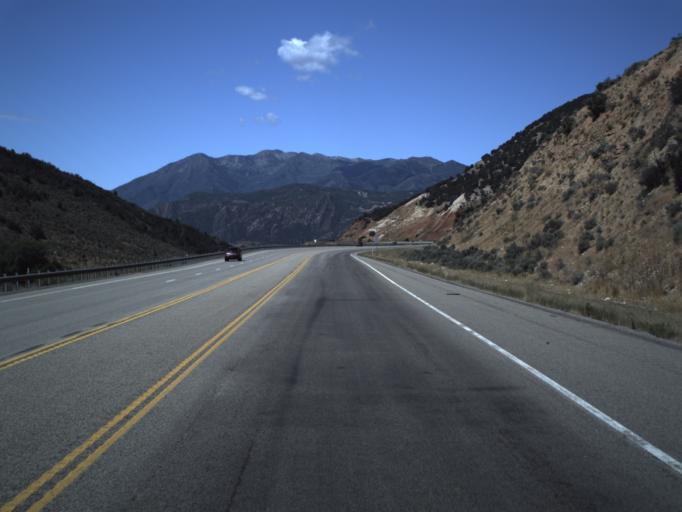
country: US
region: Utah
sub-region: Utah County
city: Mapleton
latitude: 39.9960
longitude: -111.4362
